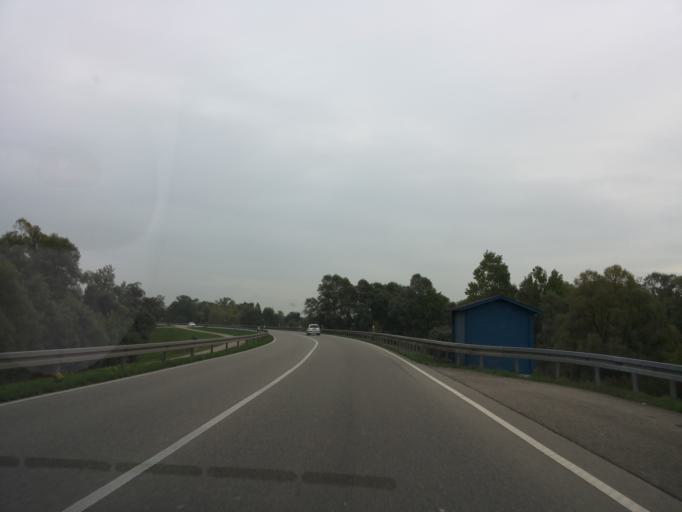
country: FR
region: Alsace
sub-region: Departement du Bas-Rhin
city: Plobsheim
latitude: 48.4947
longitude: 7.7852
